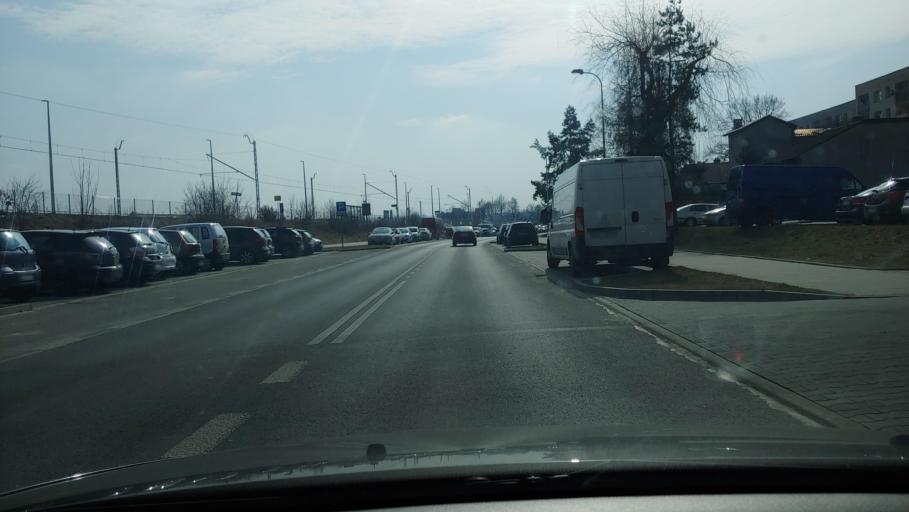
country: PL
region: Lesser Poland Voivodeship
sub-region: Powiat chrzanowski
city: Chrzanow
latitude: 50.1457
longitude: 19.4141
